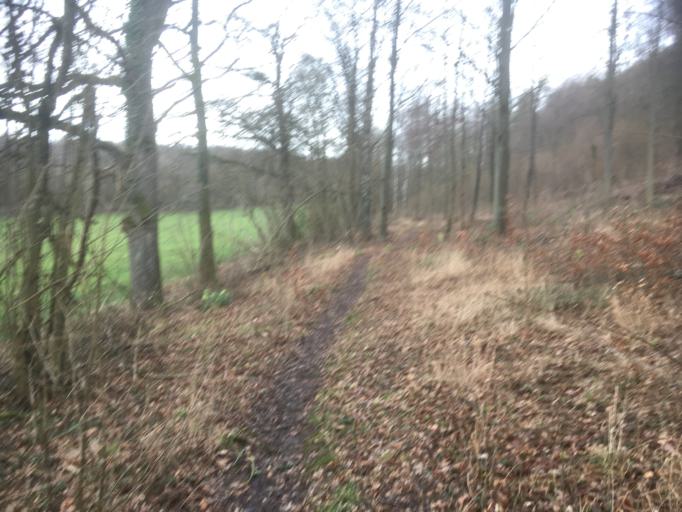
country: BE
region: Wallonia
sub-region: Province du Luxembourg
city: Durbuy
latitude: 50.3092
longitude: 5.4926
